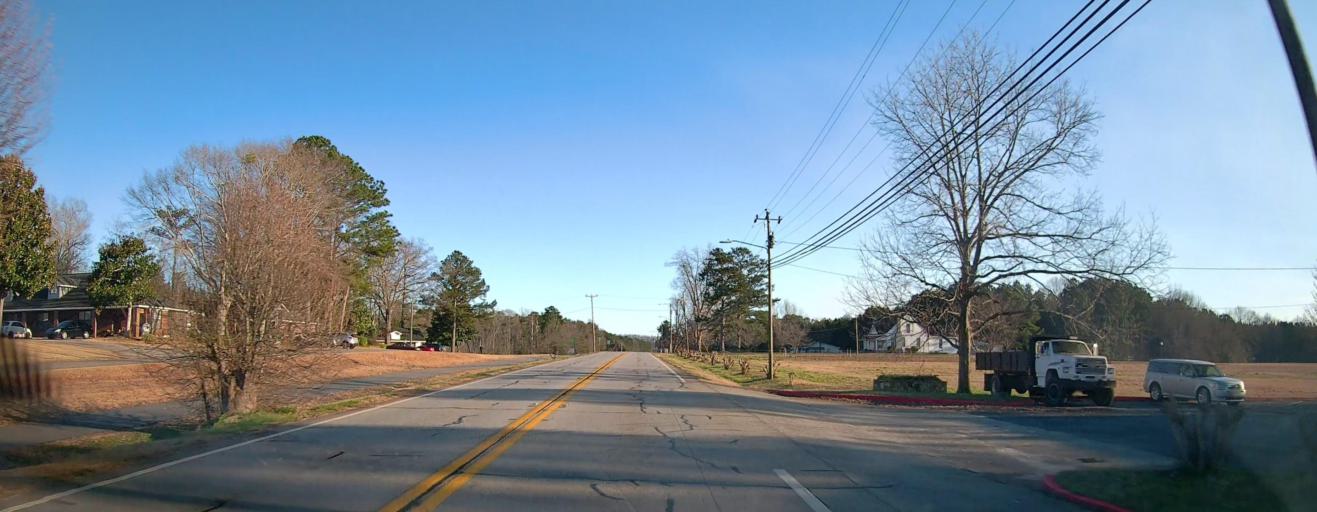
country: US
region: Georgia
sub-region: Harris County
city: Pine Mountain
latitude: 32.8586
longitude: -84.8506
